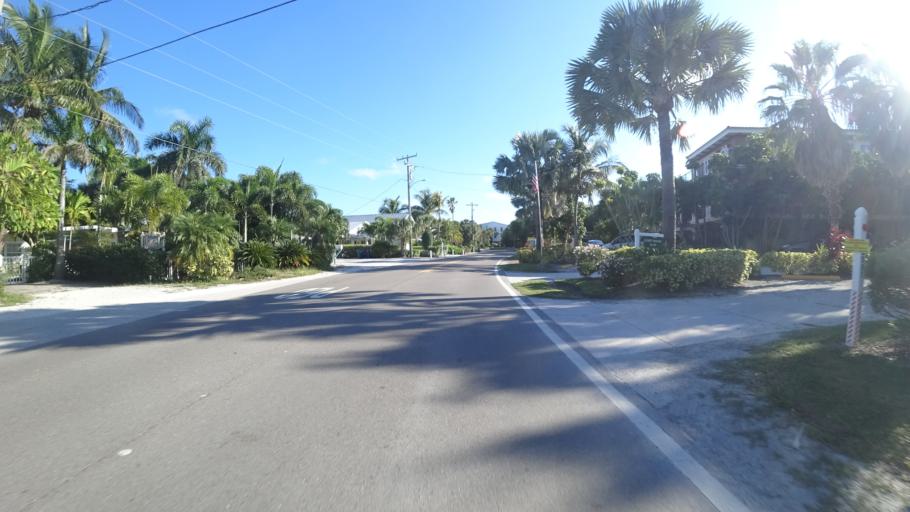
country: US
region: Florida
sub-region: Manatee County
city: Holmes Beach
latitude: 27.5093
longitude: -82.7194
